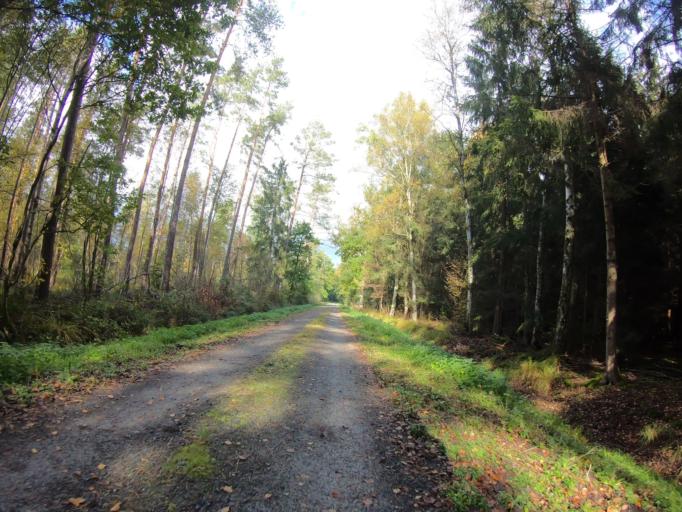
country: DE
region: Lower Saxony
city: Wahrenholz
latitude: 52.5892
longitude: 10.6302
